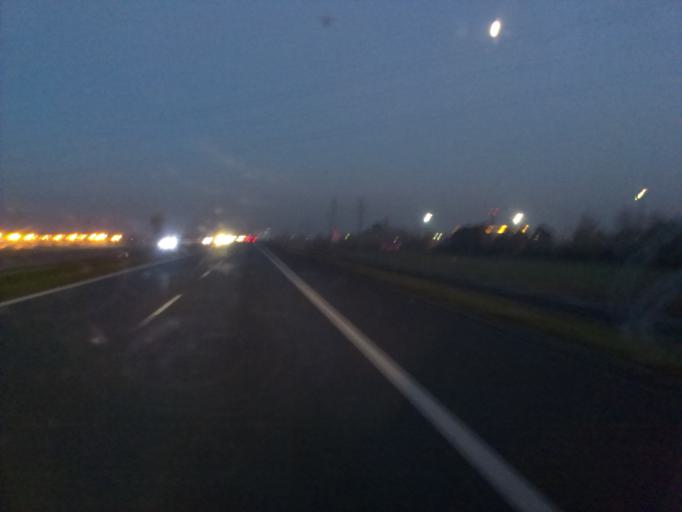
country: PL
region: Silesian Voivodeship
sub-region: Gliwice
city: Gliwice
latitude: 50.2589
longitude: 18.6874
